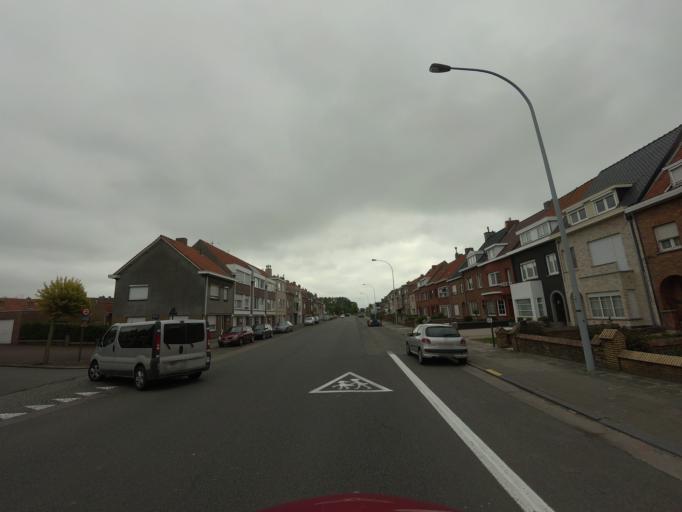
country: BE
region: Flanders
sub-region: Provincie West-Vlaanderen
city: Knokke-Heist
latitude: 51.3371
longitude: 3.2337
